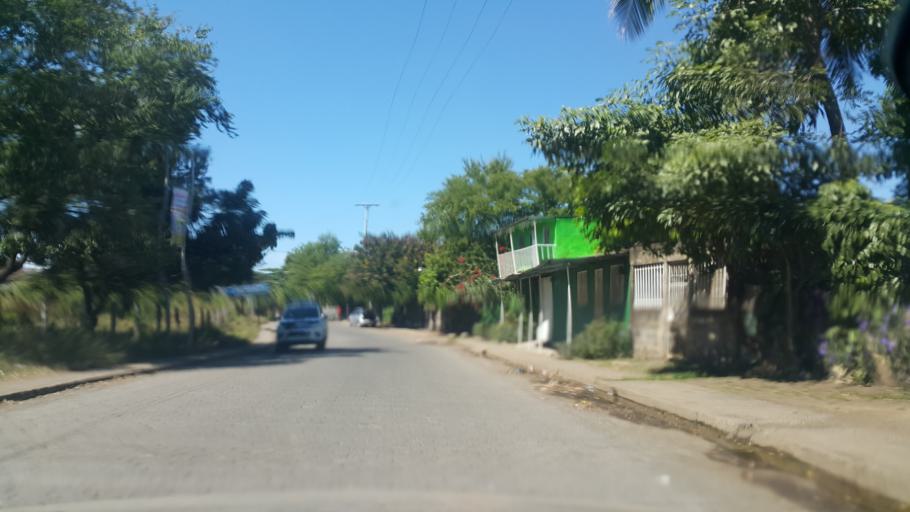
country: NI
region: Managua
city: Ciudad Sandino
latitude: 12.1474
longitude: -86.3423
